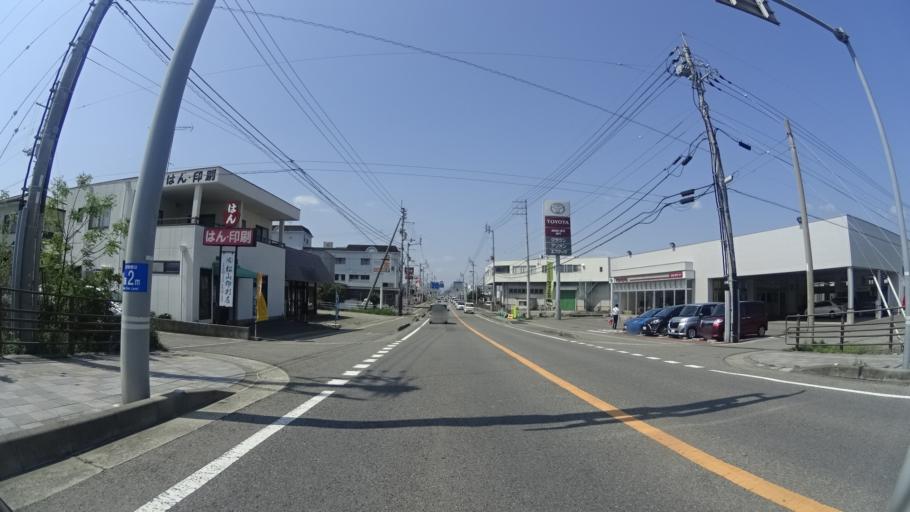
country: JP
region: Tokushima
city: Narutocho-mitsuishi
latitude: 34.1683
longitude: 134.6013
